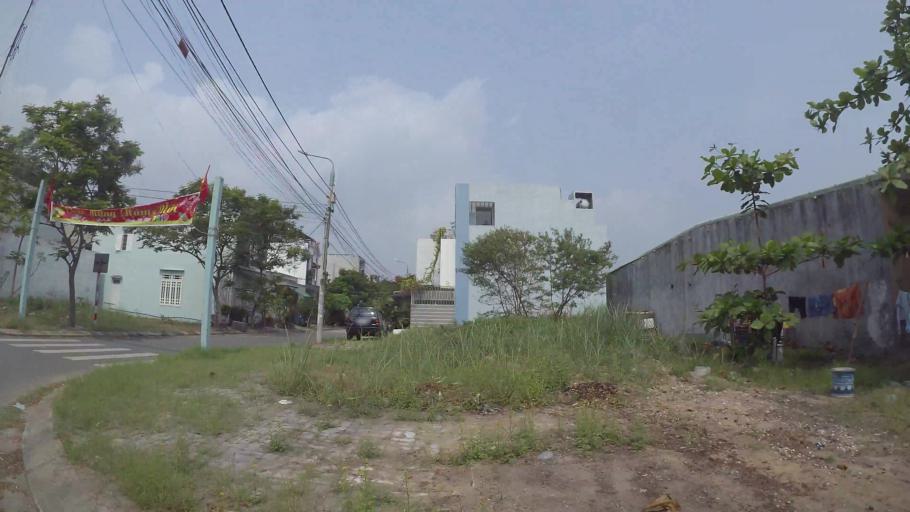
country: VN
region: Da Nang
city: Da Nang
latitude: 16.0904
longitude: 108.2383
